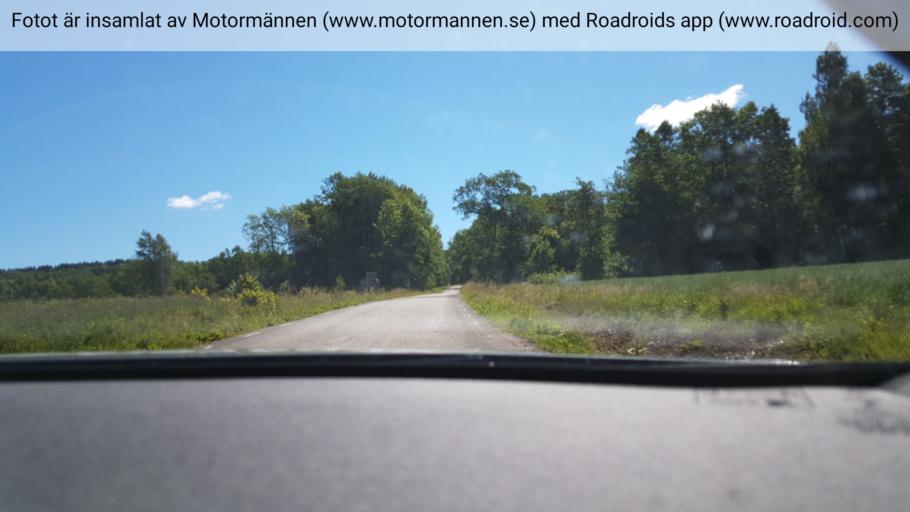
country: SE
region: Vaestra Goetaland
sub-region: Falkopings Kommun
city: Akarp
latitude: 58.1914
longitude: 13.7333
